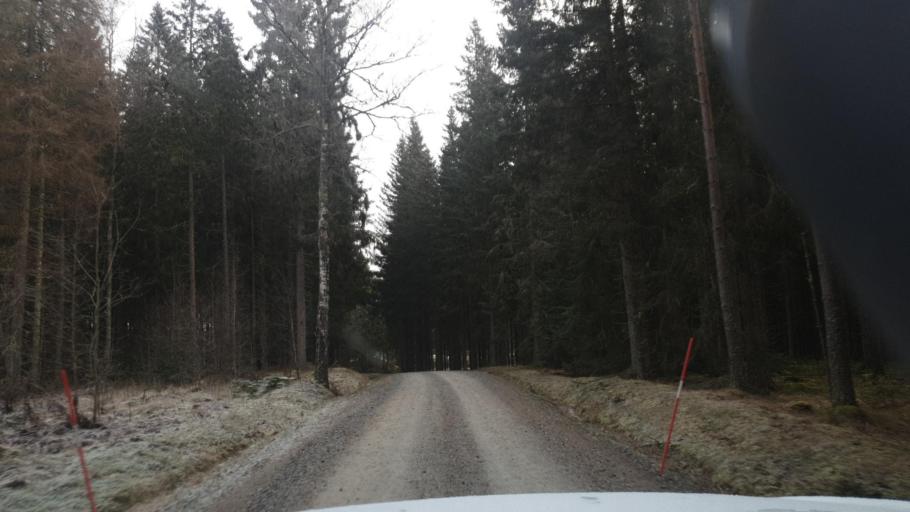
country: SE
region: Vaermland
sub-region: Karlstads Kommun
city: Edsvalla
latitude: 59.4621
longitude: 13.1052
